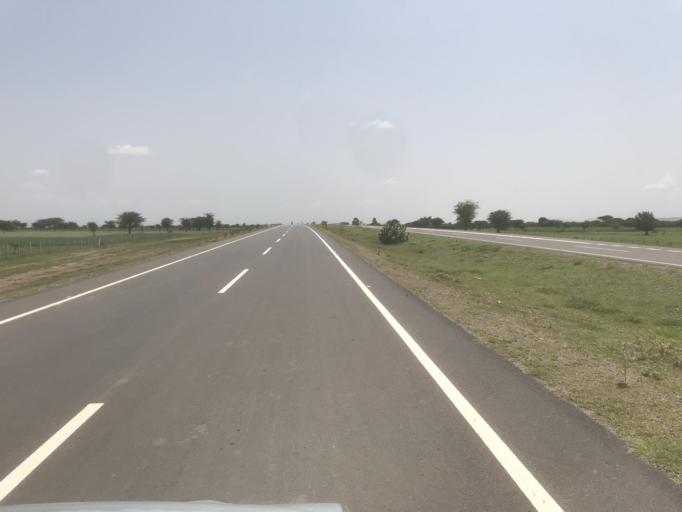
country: ET
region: Oromiya
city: Ziway
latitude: 8.2651
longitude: 38.9035
